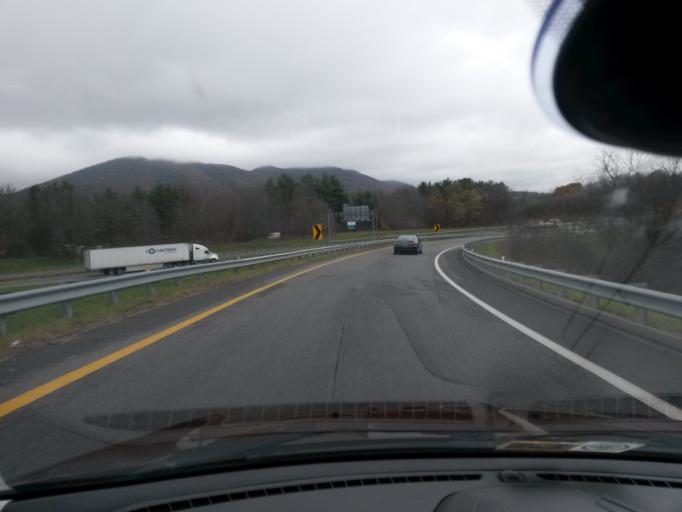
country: US
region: Virginia
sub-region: Wythe County
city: Wytheville
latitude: 36.9465
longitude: -80.9178
